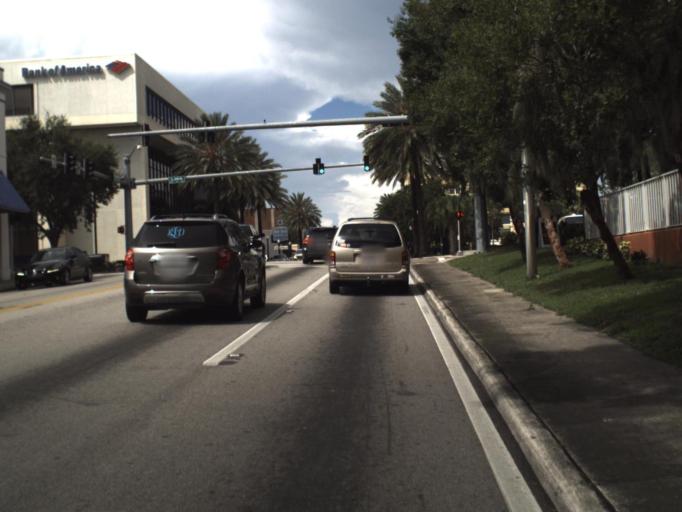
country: US
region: Florida
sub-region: Polk County
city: Lakeland
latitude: 28.0400
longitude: -81.9571
